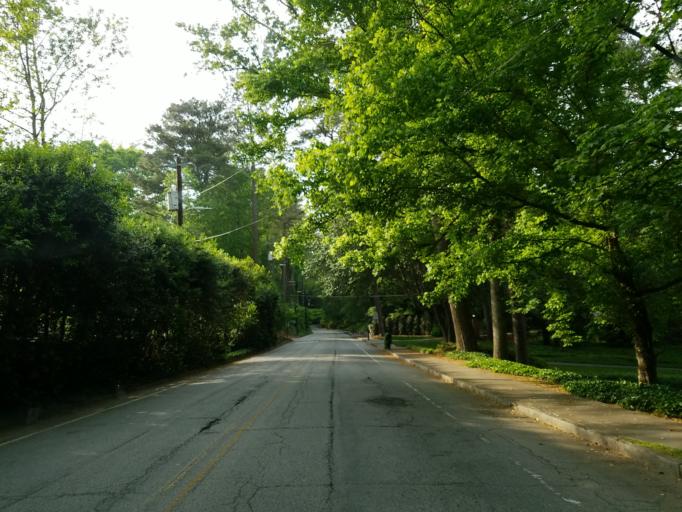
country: US
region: Georgia
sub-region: Cobb County
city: Vinings
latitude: 33.8319
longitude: -84.4175
